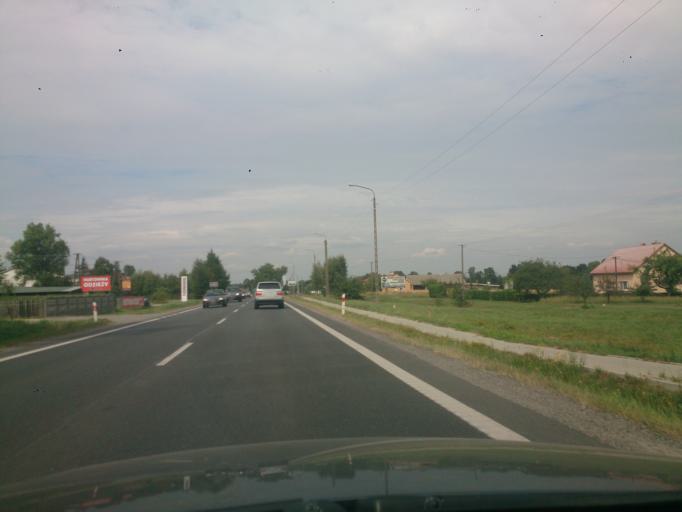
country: PL
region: Subcarpathian Voivodeship
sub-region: Powiat kolbuszowski
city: Kolbuszowa
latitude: 50.2132
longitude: 21.8176
